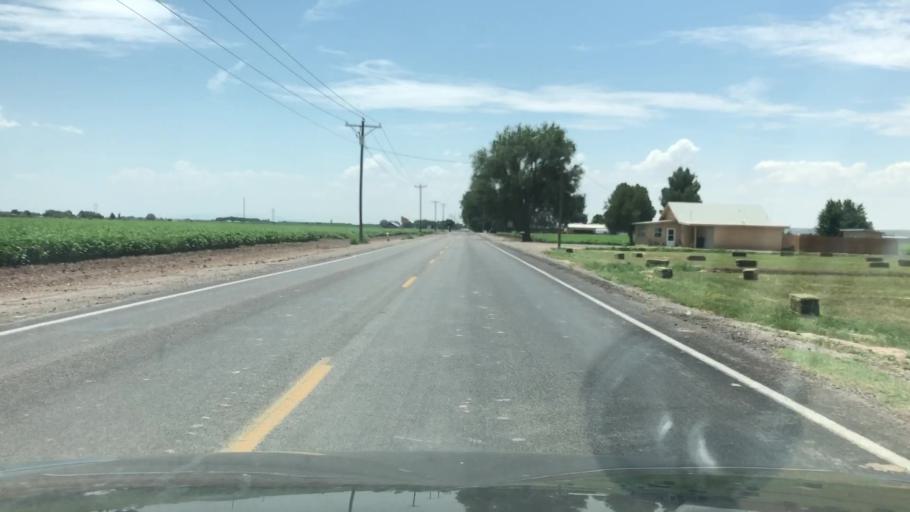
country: US
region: New Mexico
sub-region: Dona Ana County
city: Vado
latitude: 32.1076
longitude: -106.6836
